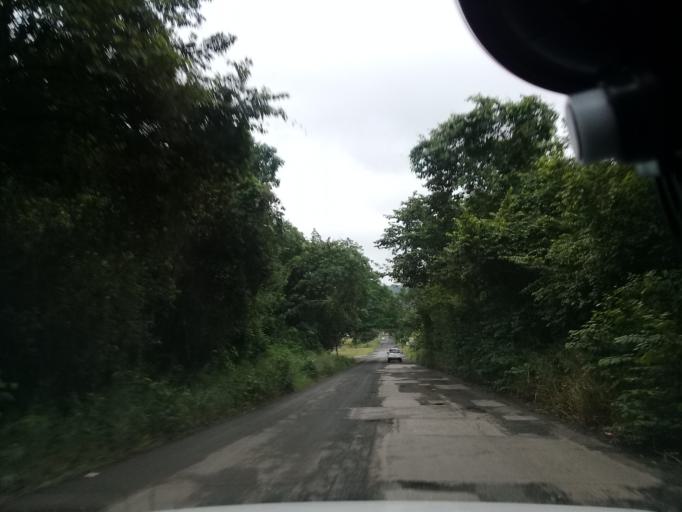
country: MX
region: Veracruz
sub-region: Chalma
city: San Pedro Coyutla
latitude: 21.2140
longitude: -98.3858
